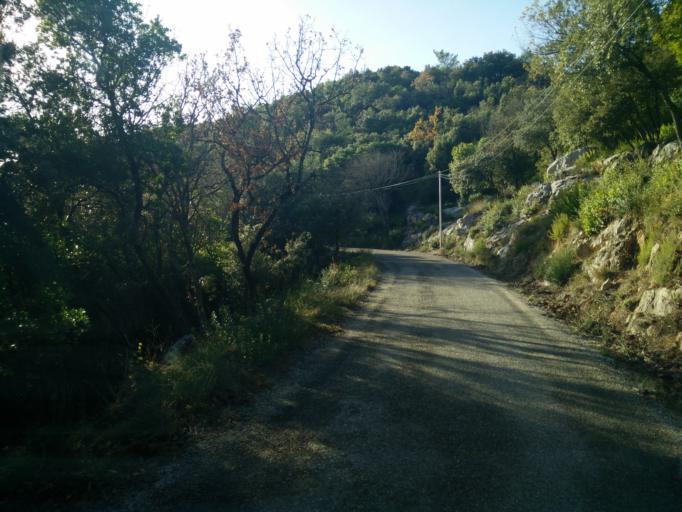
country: FR
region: Provence-Alpes-Cote d'Azur
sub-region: Departement du Var
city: Belgentier
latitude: 43.2169
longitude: 5.9764
